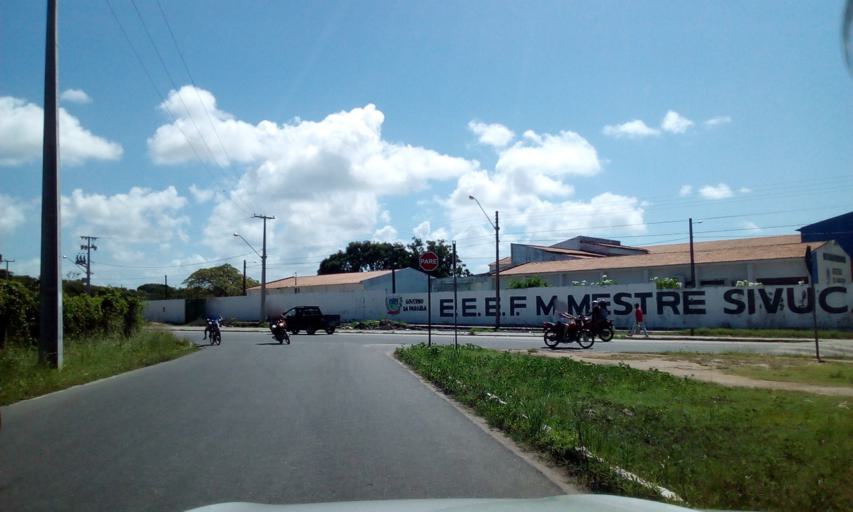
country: BR
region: Paraiba
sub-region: Joao Pessoa
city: Joao Pessoa
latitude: -7.1778
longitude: -34.8222
